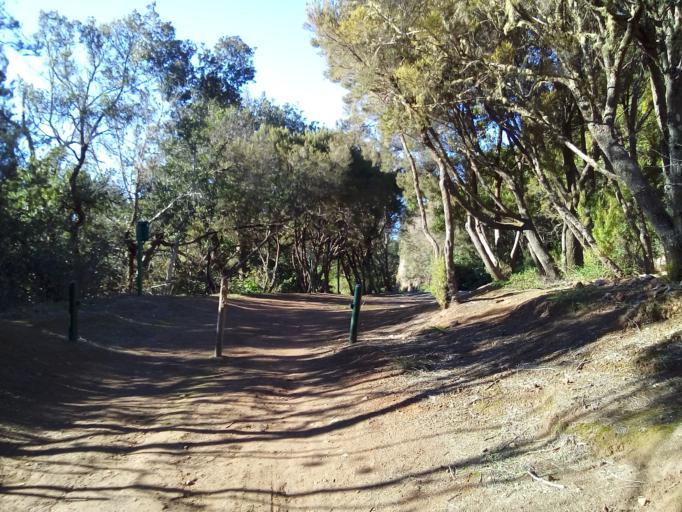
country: ES
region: Canary Islands
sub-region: Provincia de Santa Cruz de Tenerife
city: Vallehermosa
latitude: 28.1240
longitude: -17.2525
